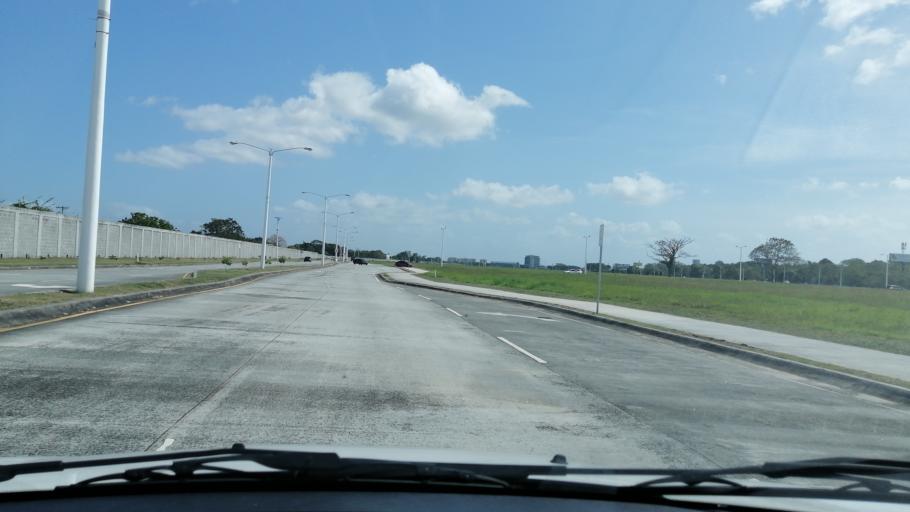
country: PA
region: Panama
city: San Miguelito
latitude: 9.0359
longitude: -79.4423
